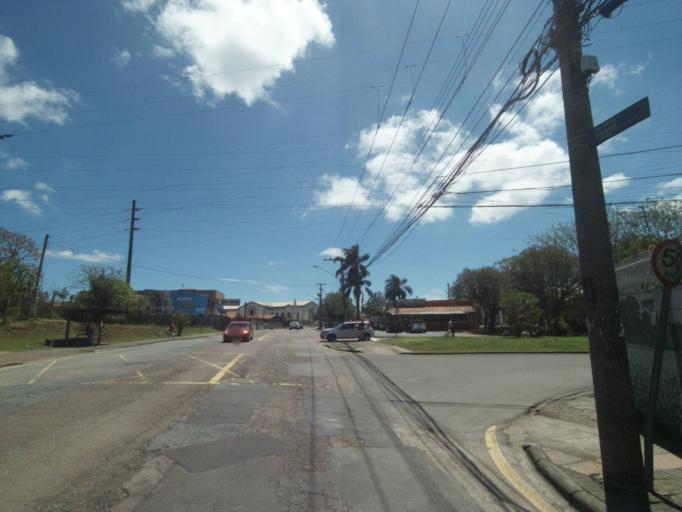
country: BR
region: Parana
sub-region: Curitiba
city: Curitiba
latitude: -25.3748
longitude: -49.2631
